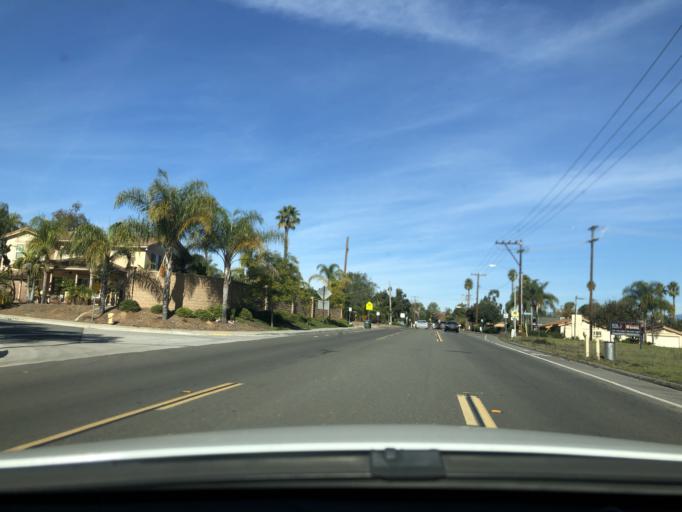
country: US
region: California
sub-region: San Diego County
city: Escondido
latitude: 33.0955
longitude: -117.0836
